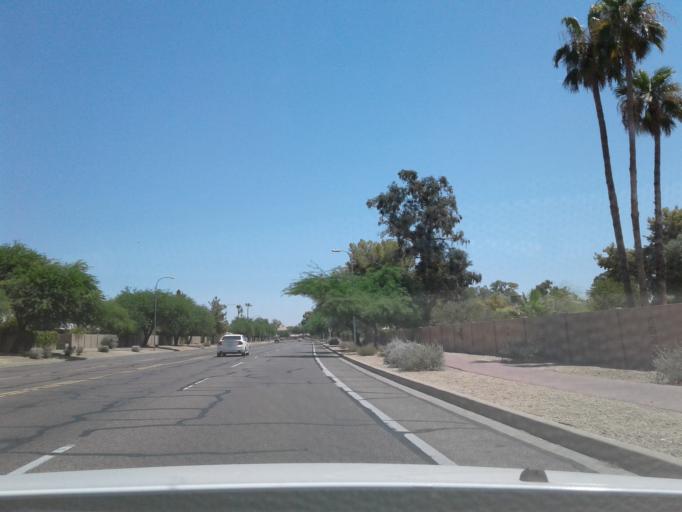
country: US
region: Arizona
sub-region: Maricopa County
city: Guadalupe
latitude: 33.3422
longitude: -111.9831
